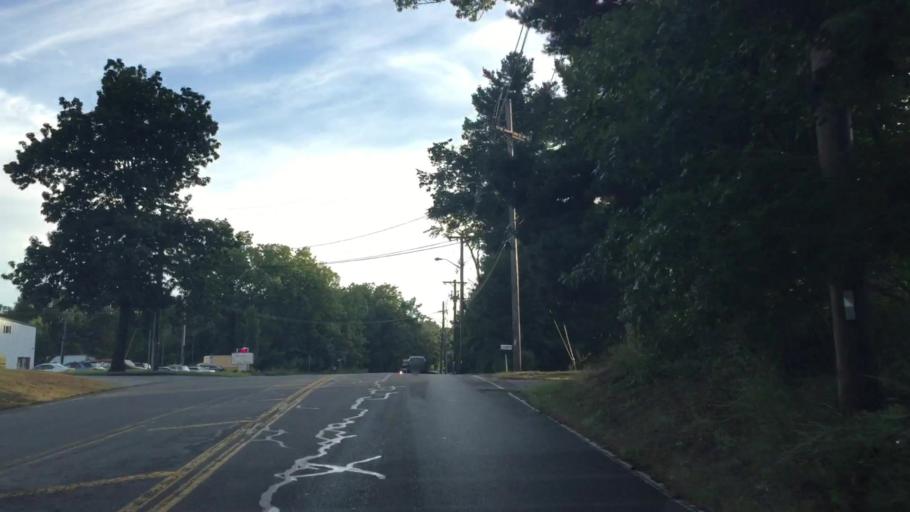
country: US
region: Massachusetts
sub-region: Middlesex County
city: Dracut
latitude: 42.7004
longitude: -71.2593
